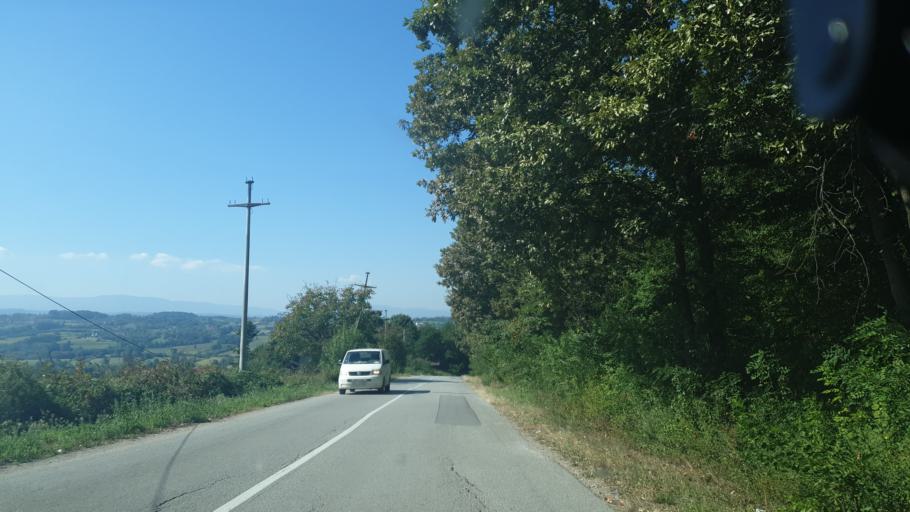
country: RS
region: Central Serbia
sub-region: Kolubarski Okrug
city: Mionica
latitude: 44.2871
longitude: 20.1228
